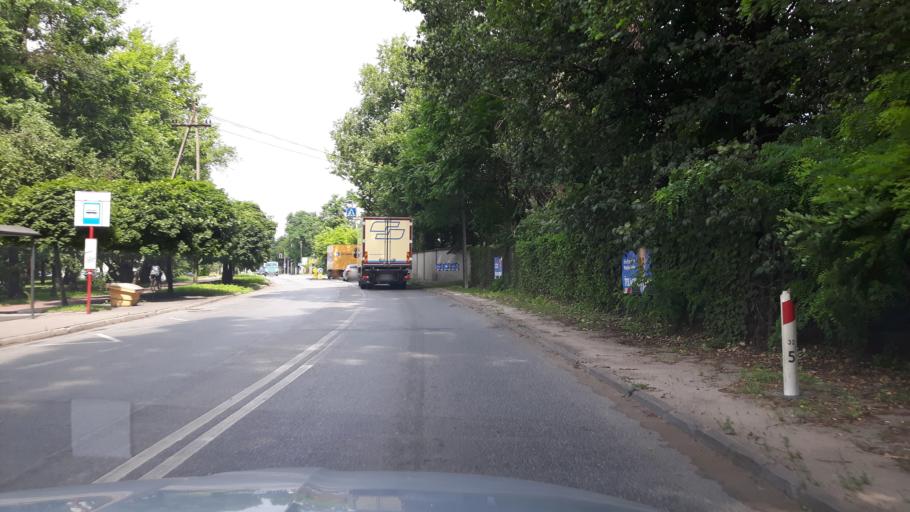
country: PL
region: Masovian Voivodeship
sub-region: Powiat wolominski
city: Nowe Lipiny
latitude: 52.3507
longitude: 21.2627
